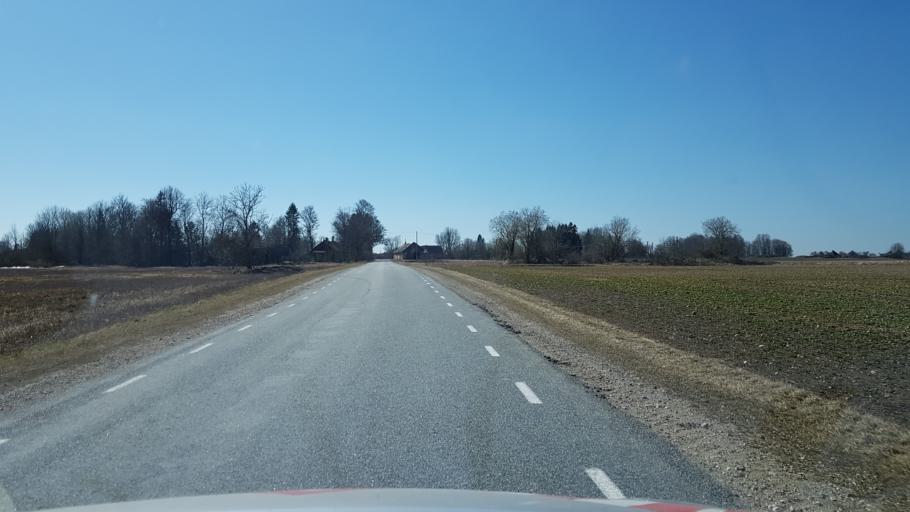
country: EE
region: Laeaene-Virumaa
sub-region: Rakke vald
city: Rakke
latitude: 59.0402
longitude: 26.3502
